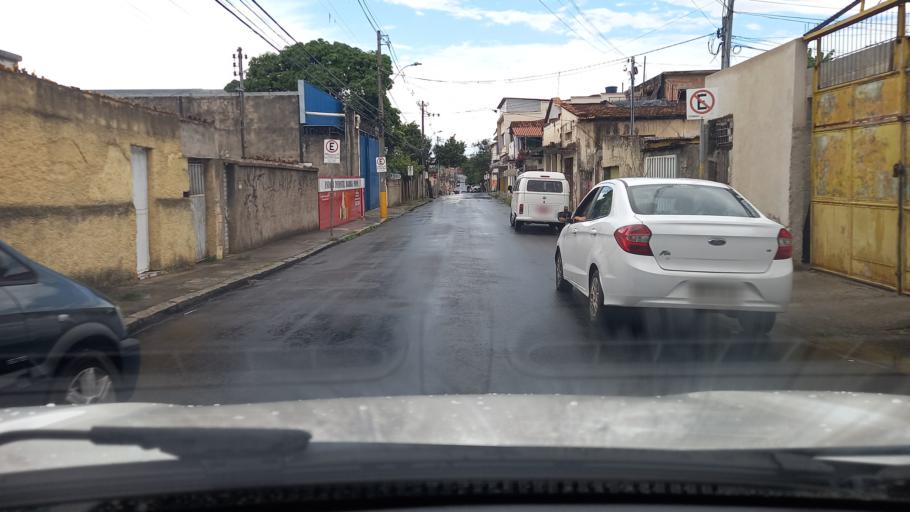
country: BR
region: Minas Gerais
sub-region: Belo Horizonte
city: Belo Horizonte
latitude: -19.9052
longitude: -43.9532
